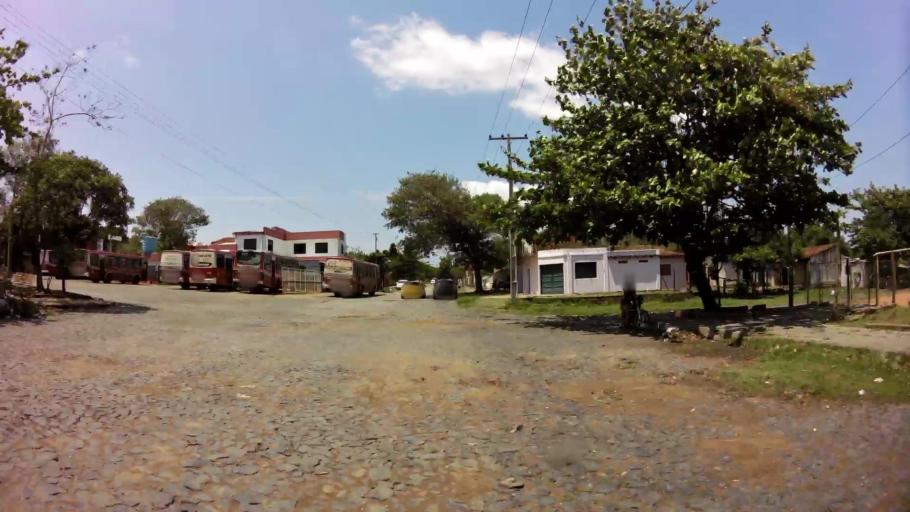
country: PY
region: Asuncion
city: Asuncion
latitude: -25.3107
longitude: -57.6427
